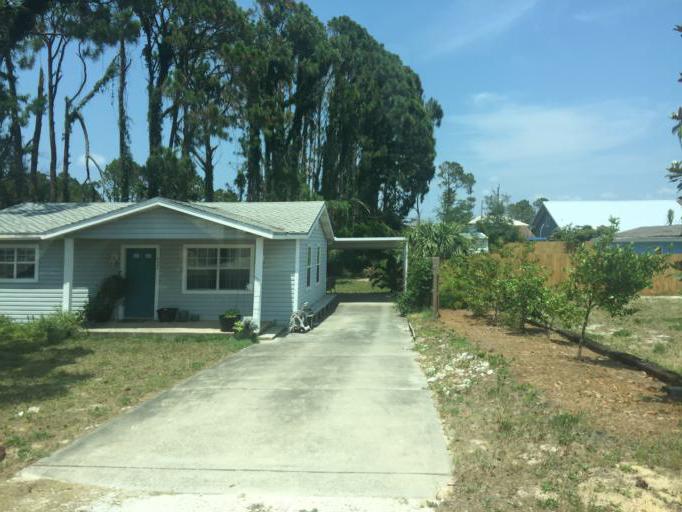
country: US
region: Florida
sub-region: Bay County
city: Lower Grand Lagoon
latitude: 30.1504
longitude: -85.7601
